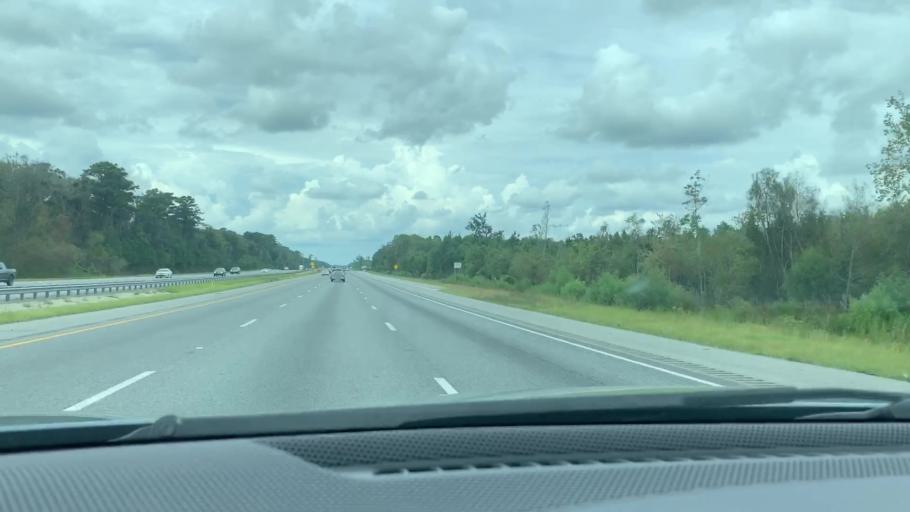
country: US
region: Georgia
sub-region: McIntosh County
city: Darien
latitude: 31.4374
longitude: -81.4441
